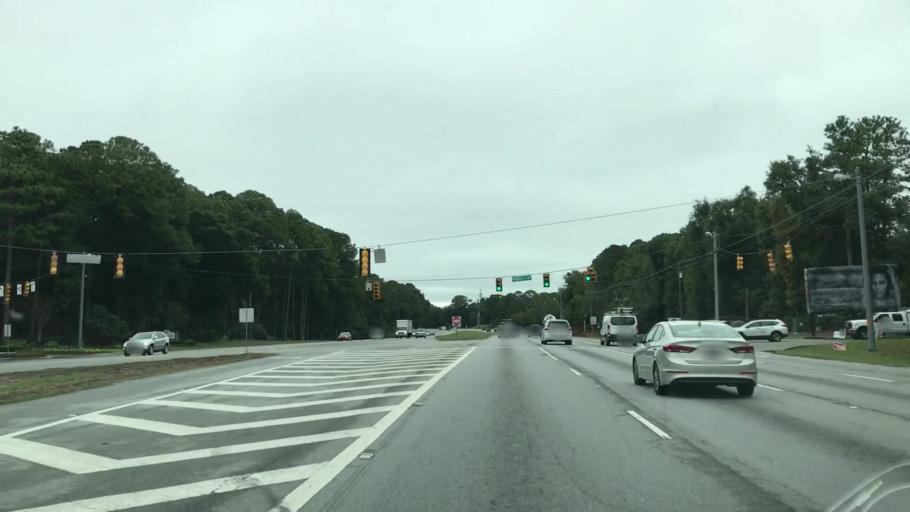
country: US
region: South Carolina
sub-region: Beaufort County
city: Bluffton
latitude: 32.2442
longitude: -80.8267
